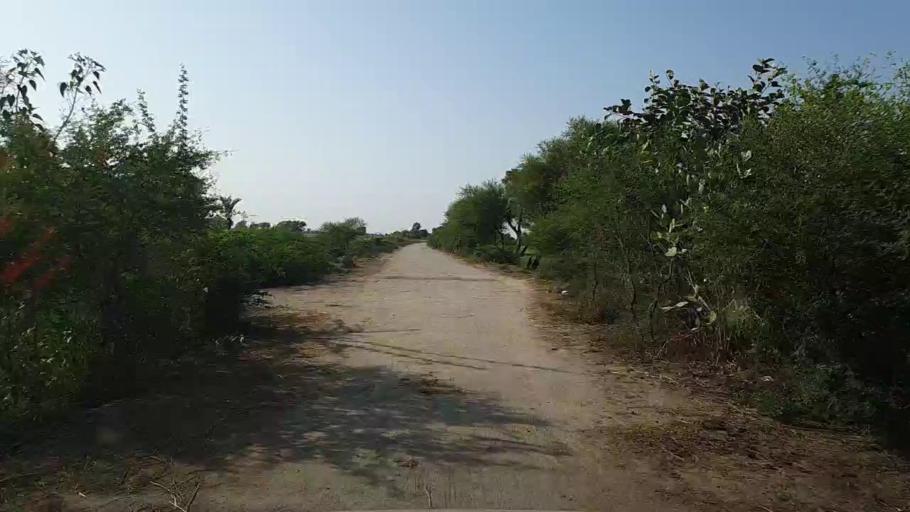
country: PK
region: Sindh
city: Kario
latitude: 24.8181
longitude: 68.4970
